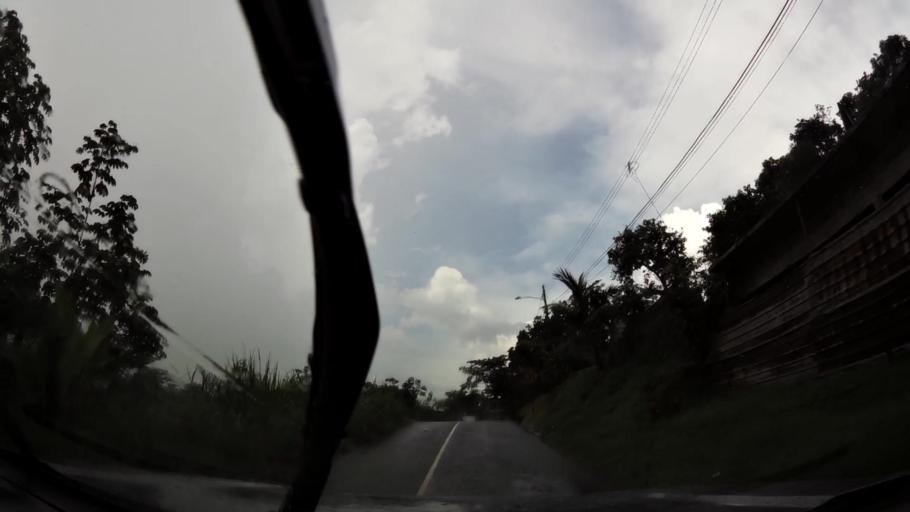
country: PA
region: Panama
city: Cabra Numero Uno
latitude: 9.1011
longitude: -79.3334
